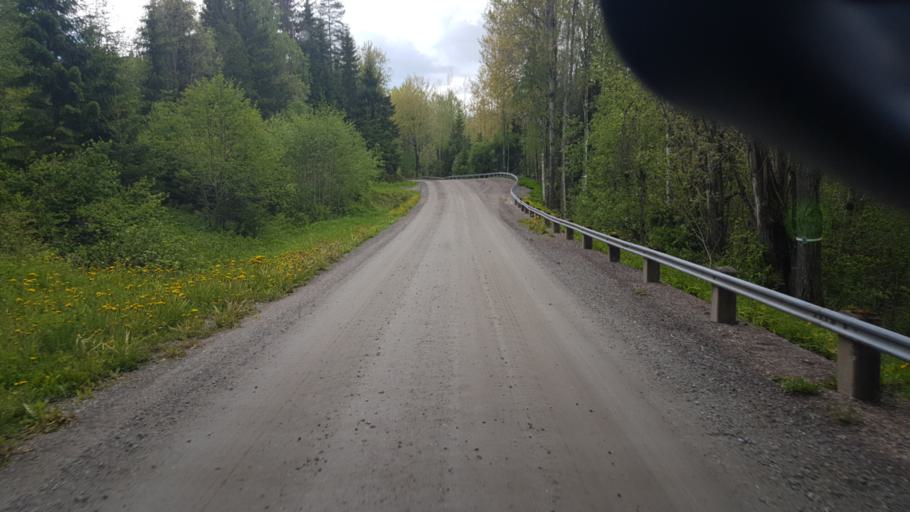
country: NO
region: Ostfold
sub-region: Romskog
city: Romskog
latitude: 59.7113
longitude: 11.9701
